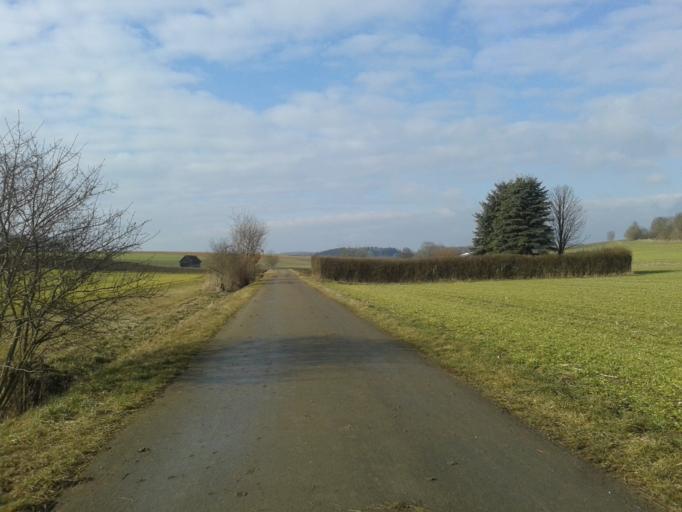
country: DE
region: Baden-Wuerttemberg
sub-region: Tuebingen Region
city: Oberdischingen
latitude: 48.3024
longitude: 9.8245
